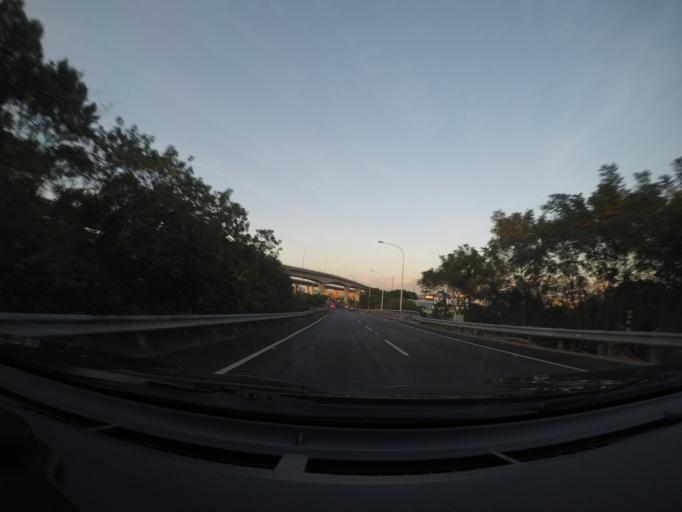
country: TW
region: Taiwan
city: Taoyuan City
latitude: 25.0201
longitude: 121.2772
